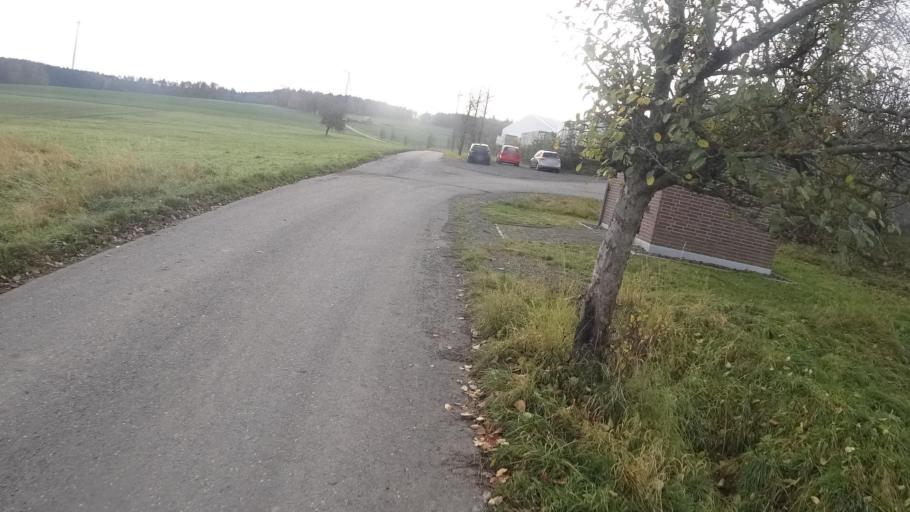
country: DE
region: Rheinland-Pfalz
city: Bickenbach
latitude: 50.1206
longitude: 7.5329
